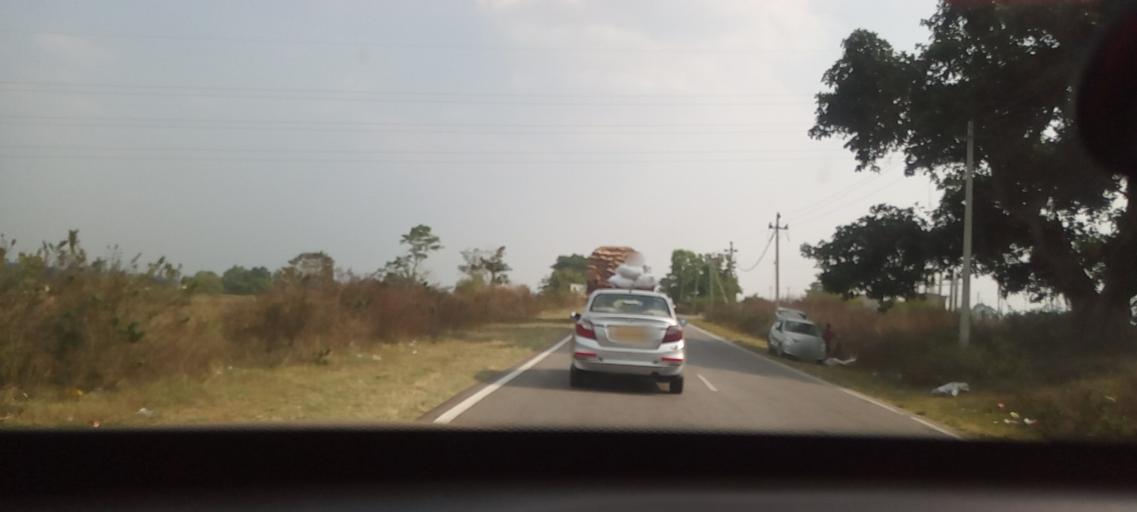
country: IN
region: Karnataka
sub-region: Hassan
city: Hassan
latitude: 13.0744
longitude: 76.0474
